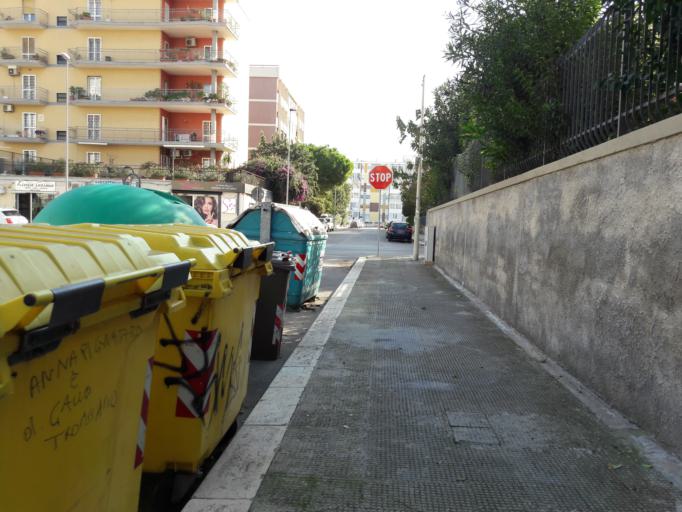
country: IT
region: Apulia
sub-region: Provincia di Bari
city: Bari
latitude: 41.1110
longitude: 16.8950
